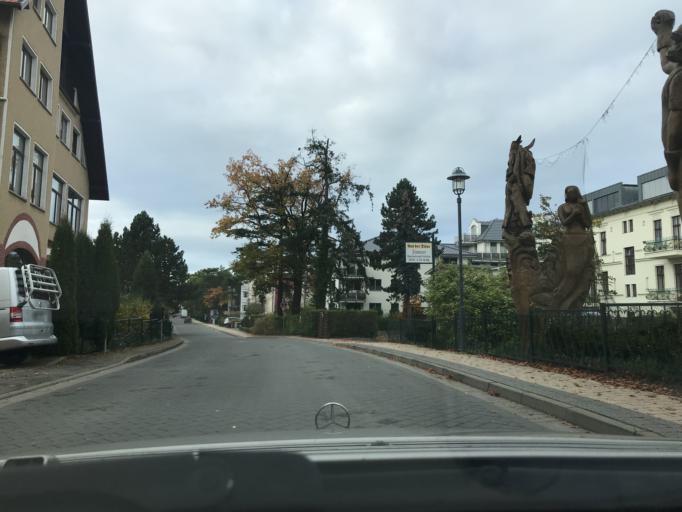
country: DE
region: Mecklenburg-Vorpommern
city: Seebad Bansin
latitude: 53.9640
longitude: 14.1556
